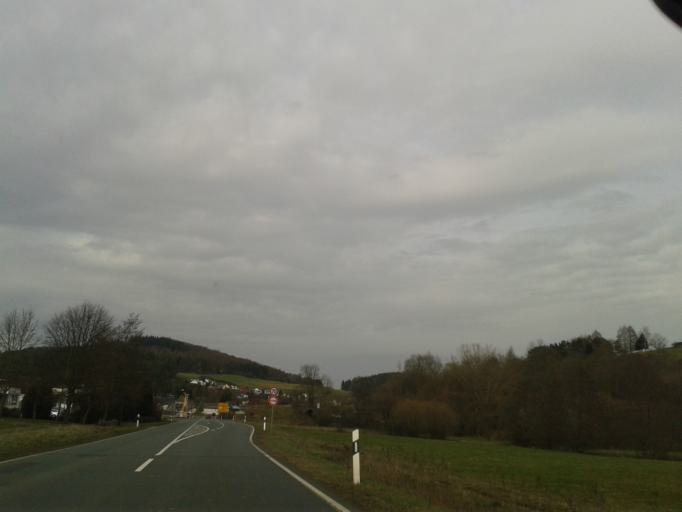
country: DE
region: Hesse
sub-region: Regierungsbezirk Giessen
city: Breidenbach
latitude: 50.8367
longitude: 8.4652
